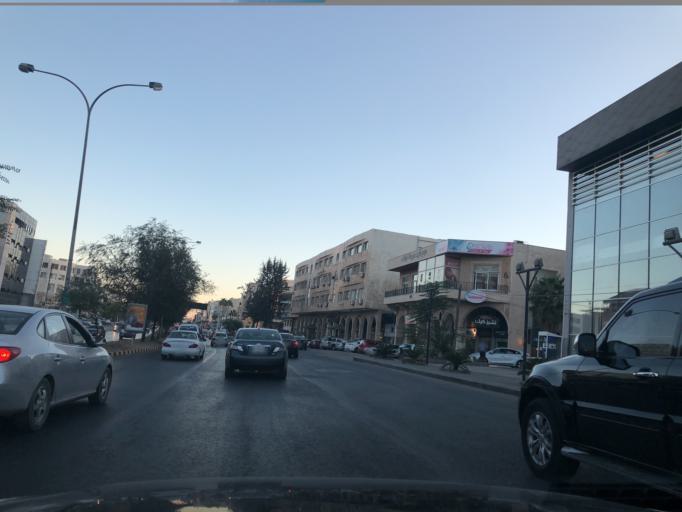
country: JO
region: Amman
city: Al Jubayhah
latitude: 32.0022
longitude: 35.8306
